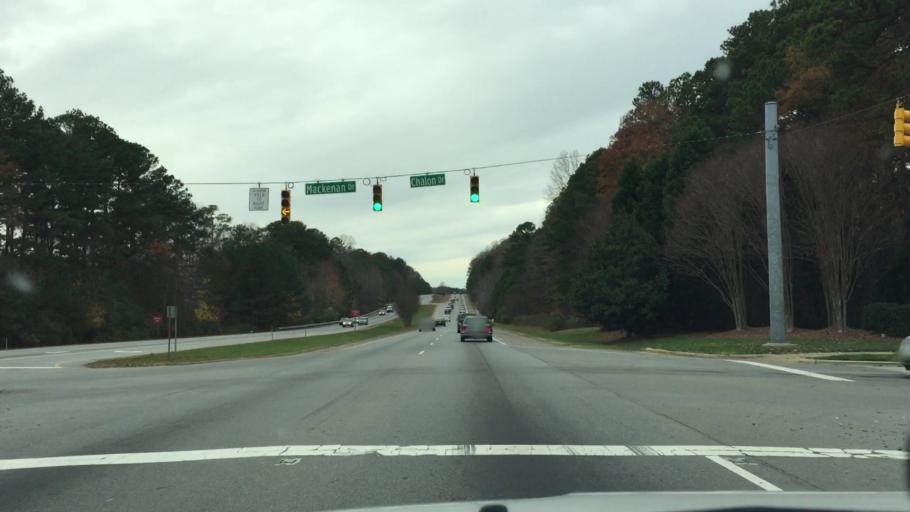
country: US
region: North Carolina
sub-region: Wake County
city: Apex
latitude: 35.7416
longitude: -78.8095
